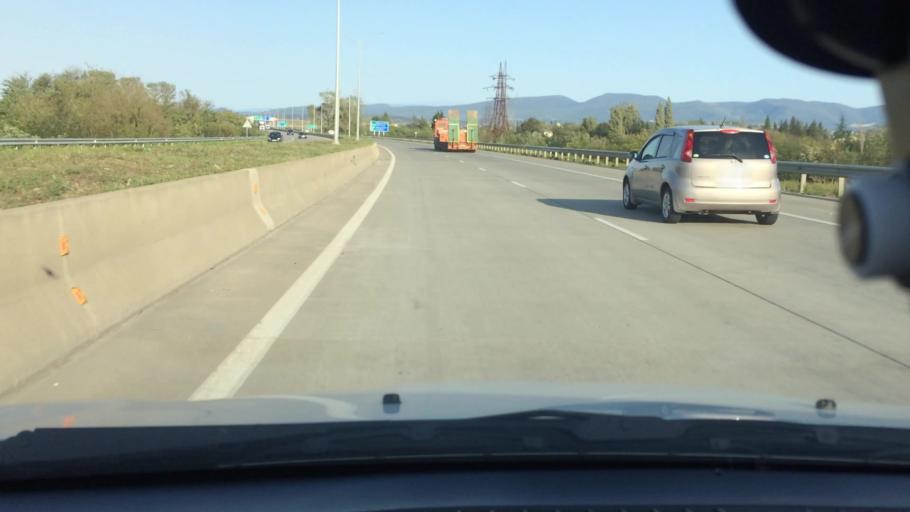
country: GE
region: Imereti
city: Zestap'oni
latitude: 42.1530
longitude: 42.9586
